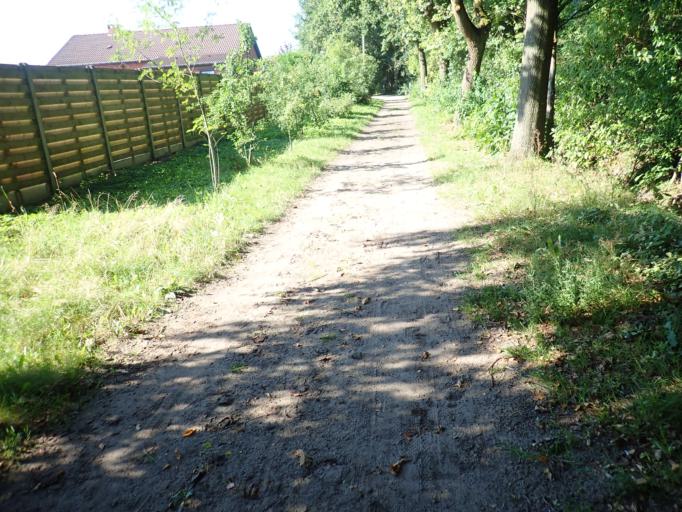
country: BE
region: Flanders
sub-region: Provincie Antwerpen
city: Westerlo
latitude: 51.0483
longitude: 4.9313
